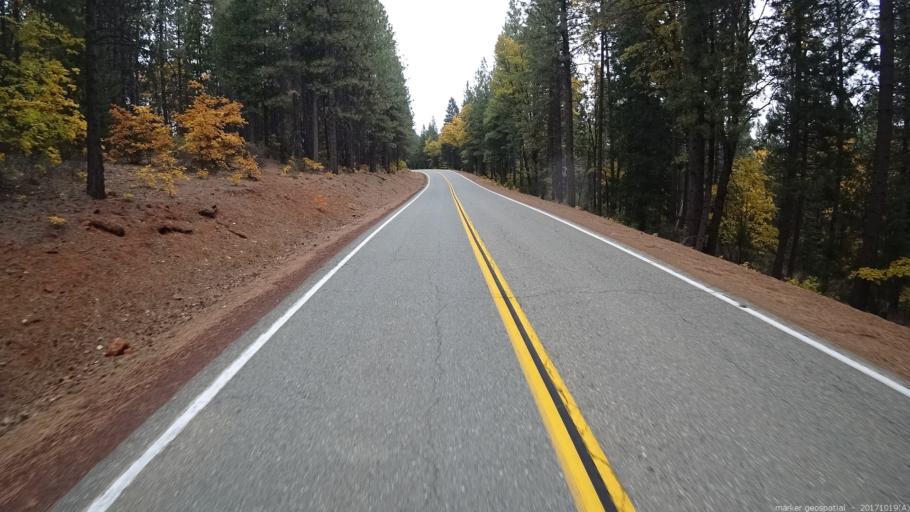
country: US
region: California
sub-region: Shasta County
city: Burney
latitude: 41.1226
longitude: -121.5907
